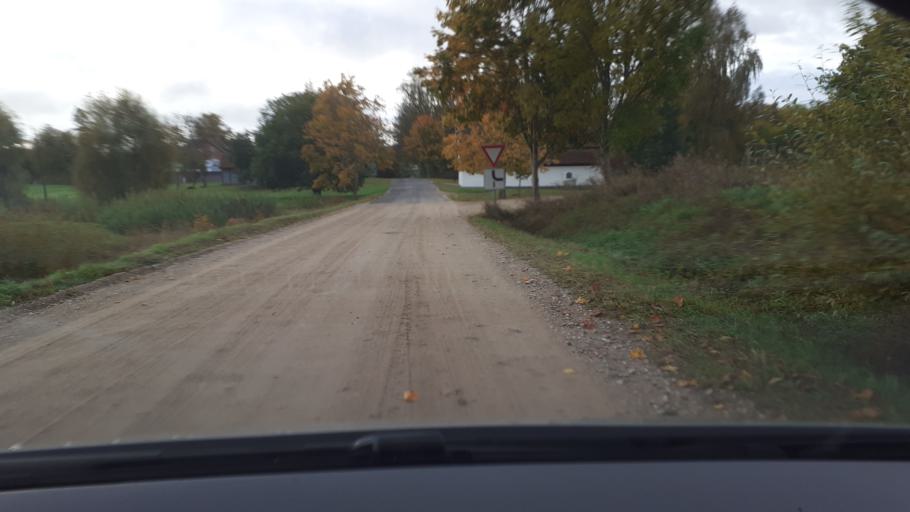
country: LV
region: Kuldigas Rajons
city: Kuldiga
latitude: 57.0208
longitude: 21.9135
